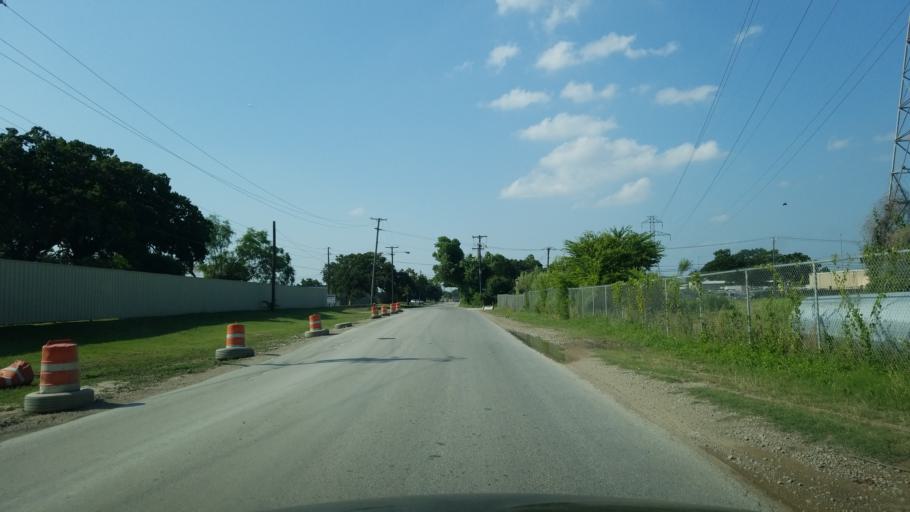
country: US
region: Texas
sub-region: Dallas County
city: Farmers Branch
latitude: 32.8853
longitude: -96.9019
